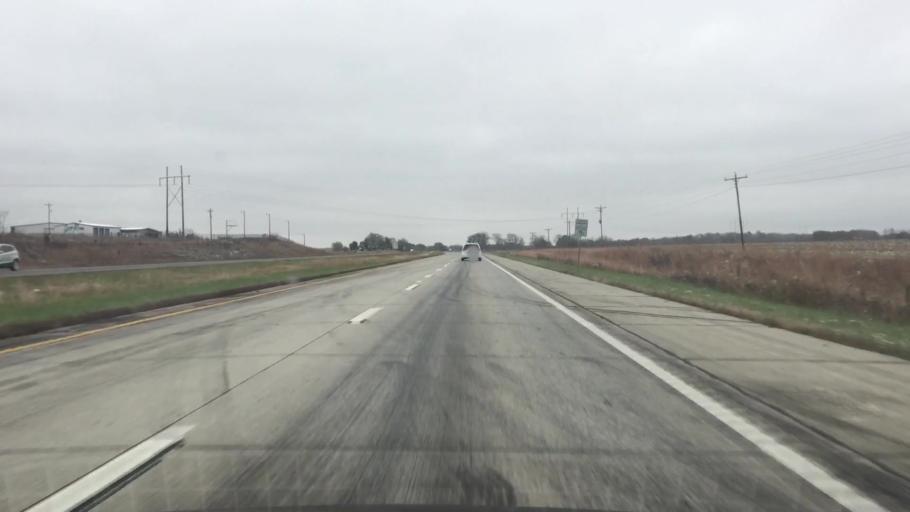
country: US
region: Missouri
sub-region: Saint Clair County
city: Osceola
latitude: 38.0341
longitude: -93.6782
